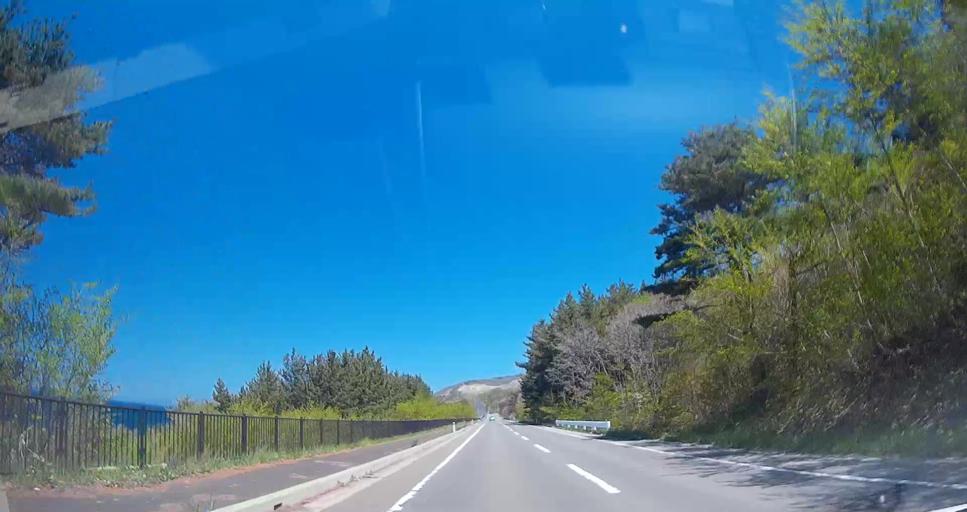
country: JP
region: Aomori
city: Mutsu
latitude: 41.3913
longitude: 141.4146
